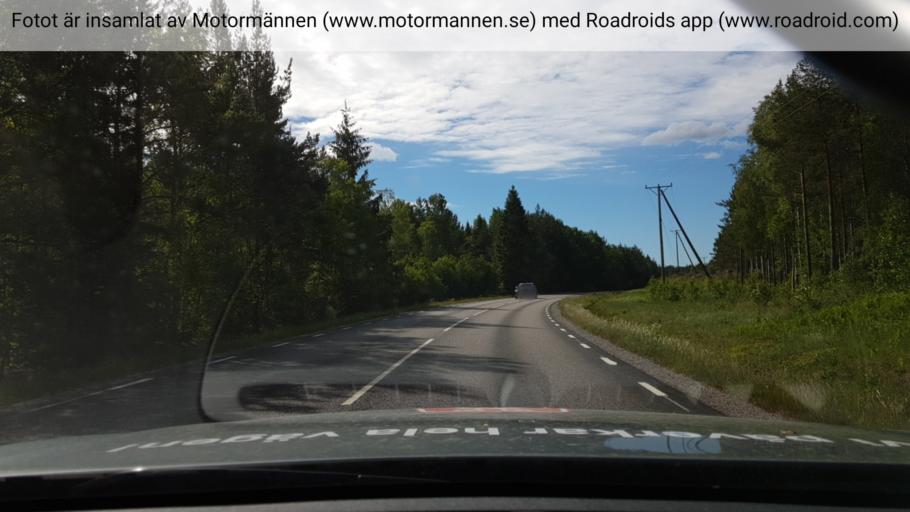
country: SE
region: Stockholm
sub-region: Nynashamns Kommun
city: Nynashamn
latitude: 58.9602
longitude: 17.9972
